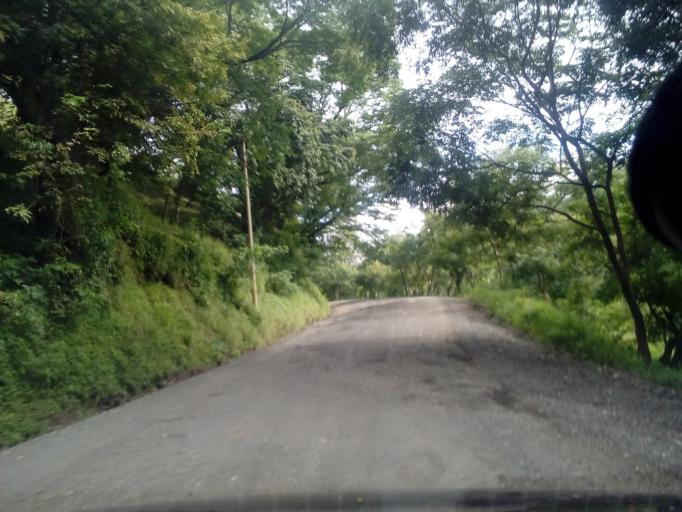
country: CR
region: Guanacaste
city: Samara
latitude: 9.9192
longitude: -85.6543
